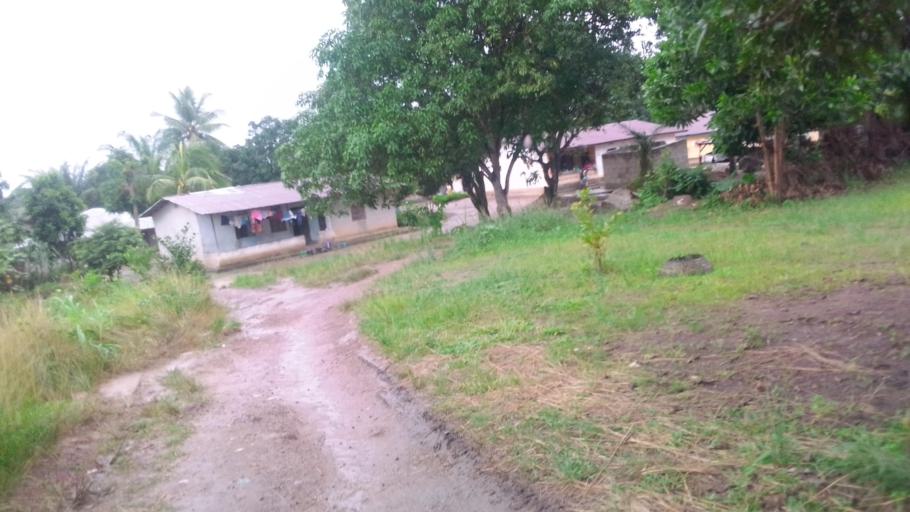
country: SL
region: Eastern Province
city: Kenema
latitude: 7.8510
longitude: -11.1832
